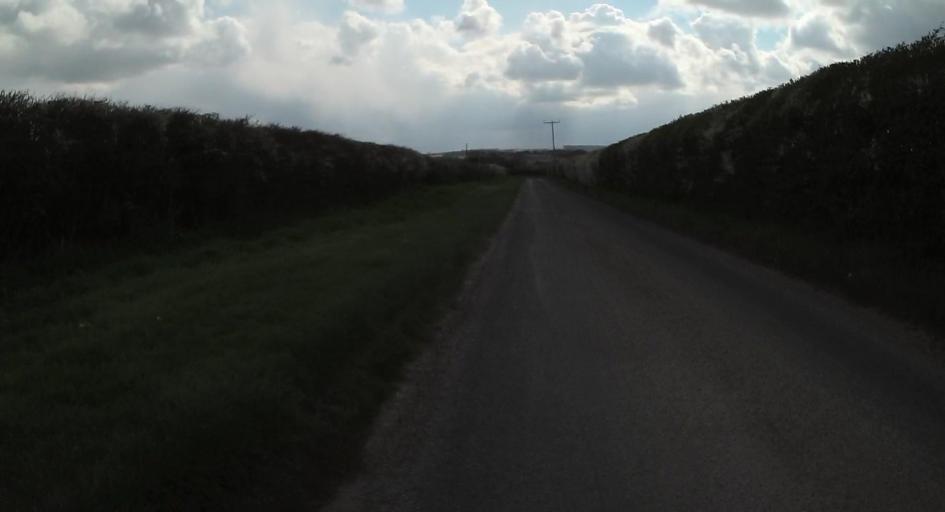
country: GB
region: England
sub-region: Hampshire
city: Kings Worthy
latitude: 51.0939
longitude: -1.2019
